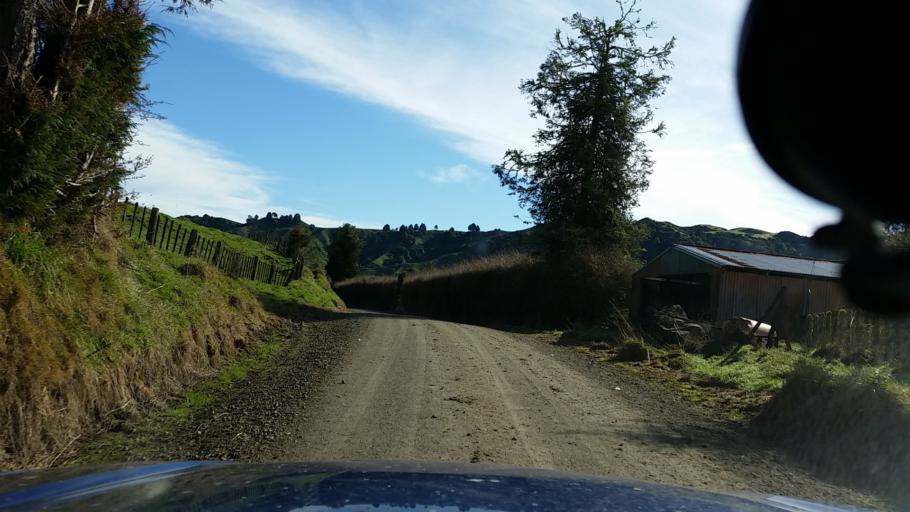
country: NZ
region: Taranaki
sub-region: New Plymouth District
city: Waitara
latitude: -39.0531
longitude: 174.7721
